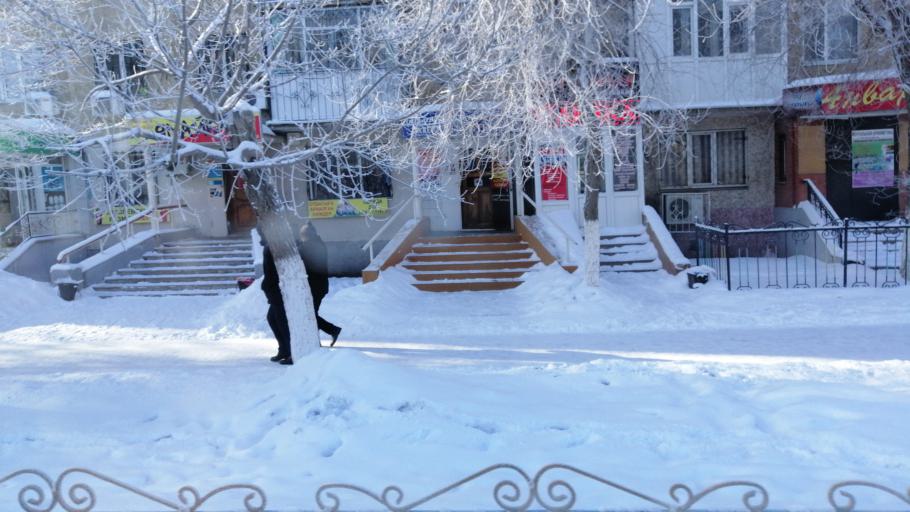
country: KZ
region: Aqtoebe
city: Aqtobe
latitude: 50.3037
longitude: 57.1521
